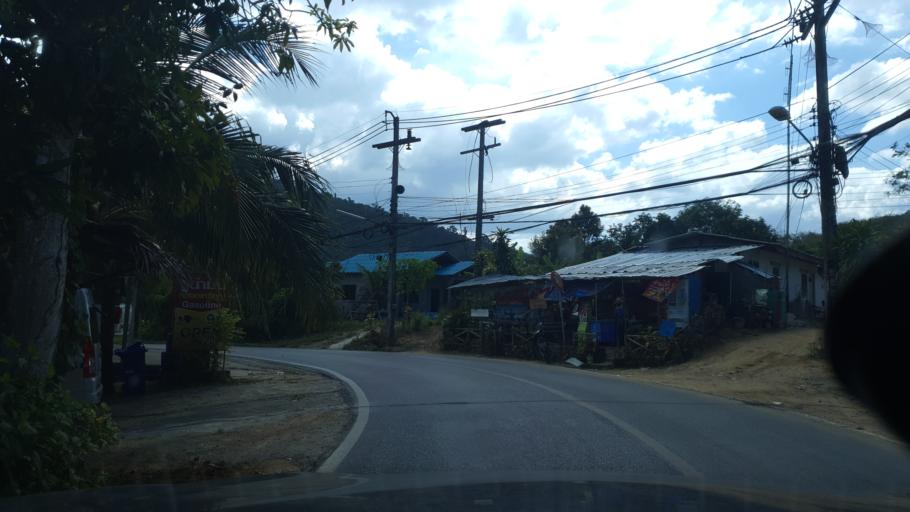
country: TH
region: Phuket
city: Thalang
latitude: 8.0704
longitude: 98.2952
